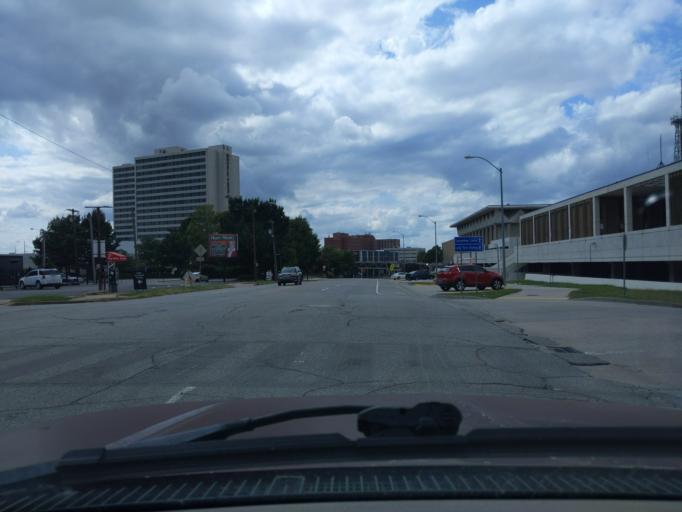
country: US
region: Oklahoma
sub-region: Tulsa County
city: Tulsa
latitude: 36.1490
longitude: -95.9941
